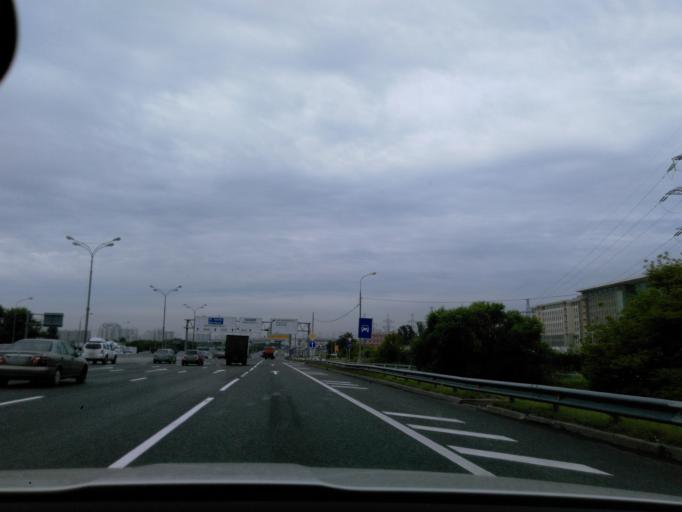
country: RU
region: Moscow
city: Veshnyaki
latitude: 55.7179
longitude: 37.8386
